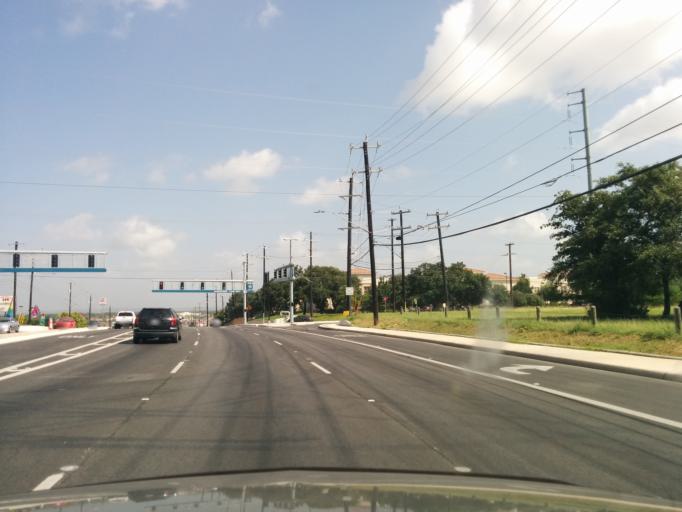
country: US
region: Texas
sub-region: Bexar County
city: Leon Valley
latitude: 29.5154
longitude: -98.5926
